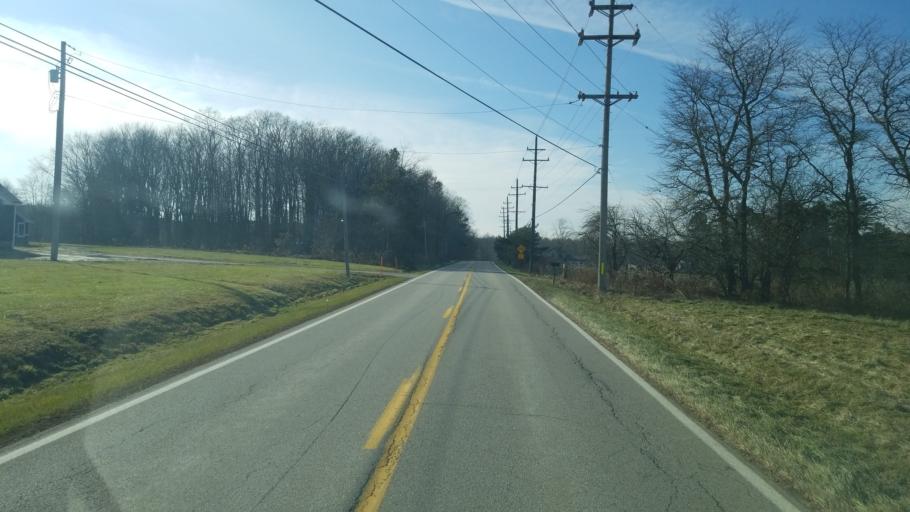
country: US
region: Ohio
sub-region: Ashtabula County
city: Jefferson
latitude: 41.7256
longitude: -80.8150
